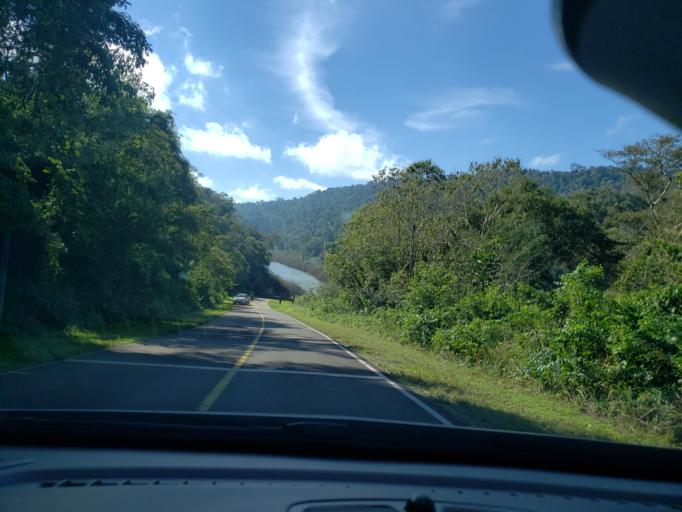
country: BR
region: Rio Grande do Sul
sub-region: Tres Passos
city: Tres Passos
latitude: -27.1456
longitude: -53.9095
